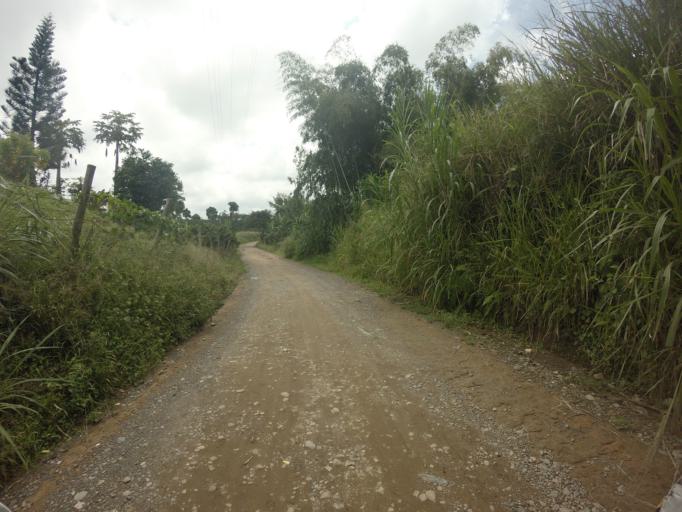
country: CO
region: Valle del Cauca
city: Ulloa
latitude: 4.6935
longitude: -75.7273
